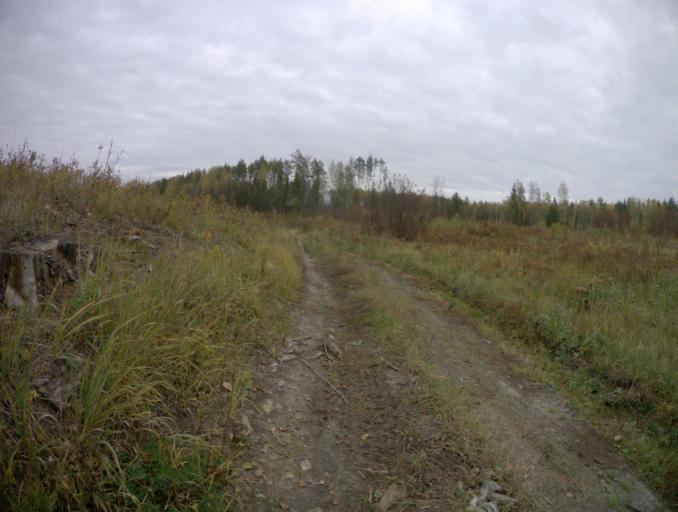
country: RU
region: Vladimir
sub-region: Kovrovskiy Rayon
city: Kovrov
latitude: 56.3146
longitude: 41.5165
